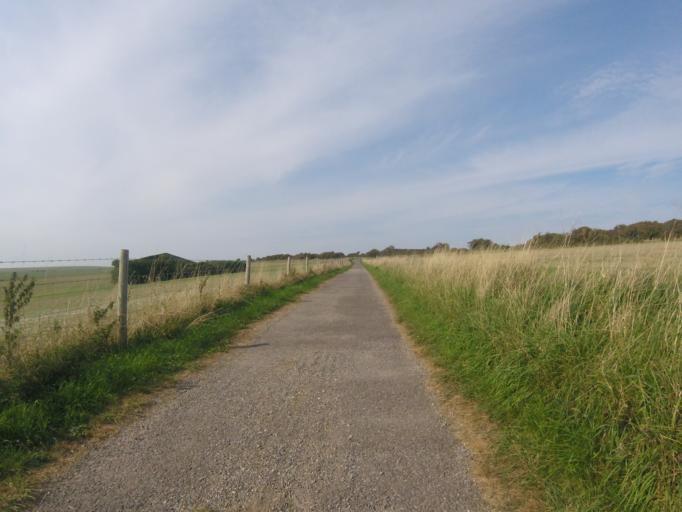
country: GB
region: England
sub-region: West Sussex
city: Fulking
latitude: 50.8734
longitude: -0.2002
